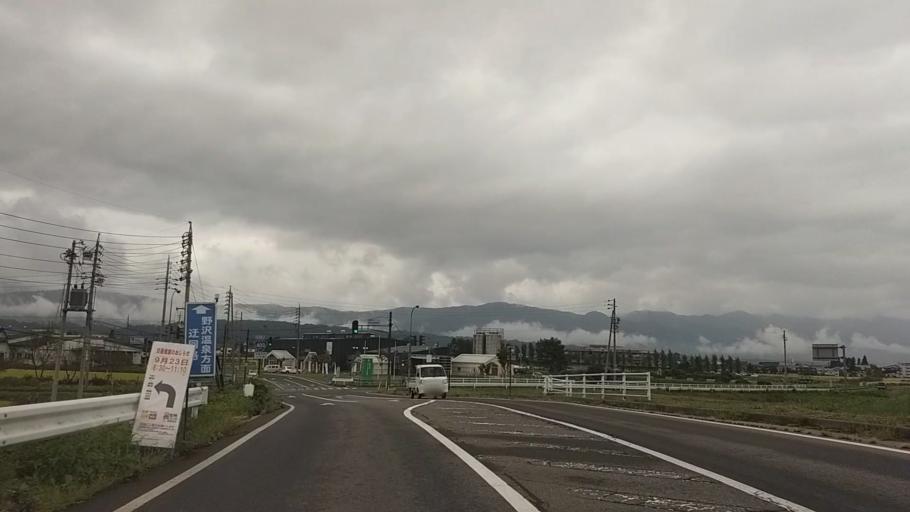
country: JP
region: Nagano
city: Iiyama
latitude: 36.8507
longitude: 138.3899
